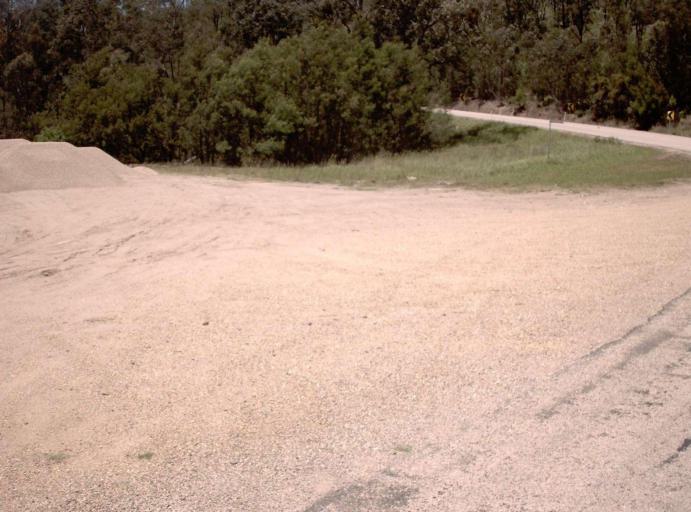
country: AU
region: Victoria
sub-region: East Gippsland
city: Bairnsdale
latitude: -37.4494
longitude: 147.8264
